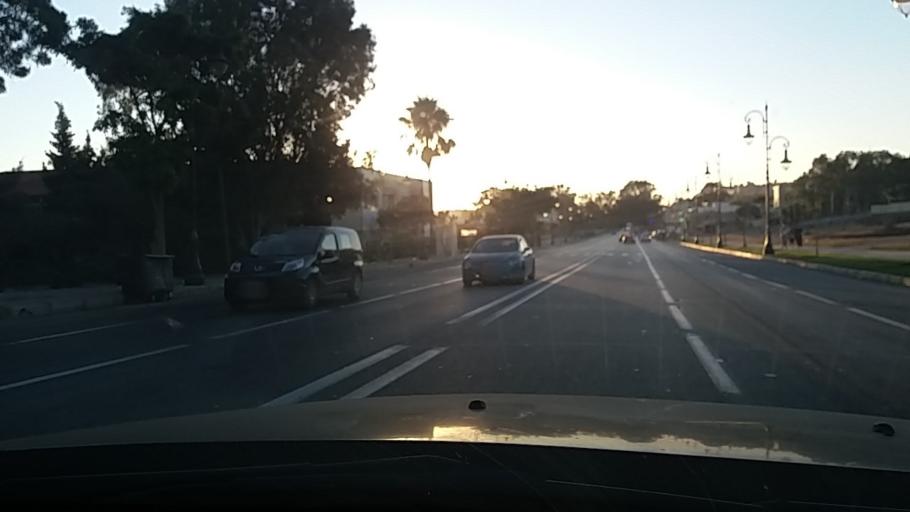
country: MA
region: Tanger-Tetouan
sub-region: Tanger-Assilah
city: Boukhalef
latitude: 35.7393
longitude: -5.8763
